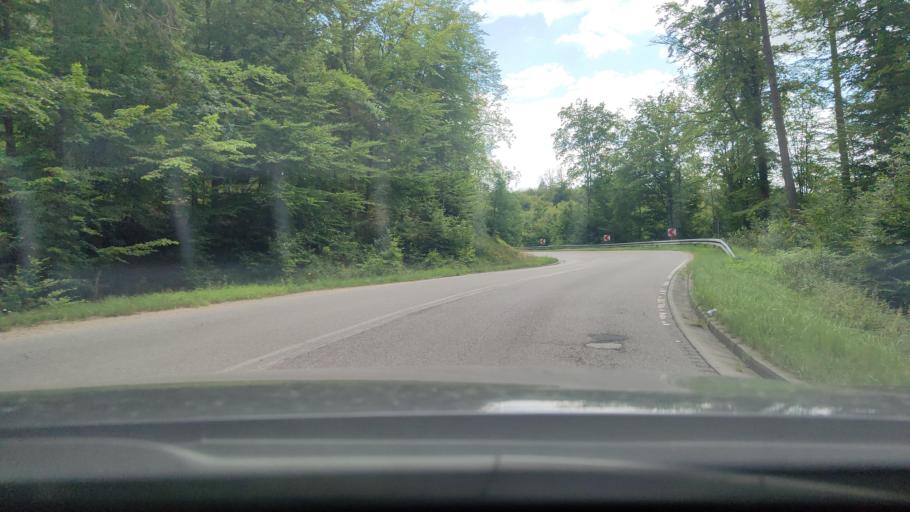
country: PL
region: Pomeranian Voivodeship
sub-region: Powiat wejherowski
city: Wejherowo
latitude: 54.5729
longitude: 18.2569
